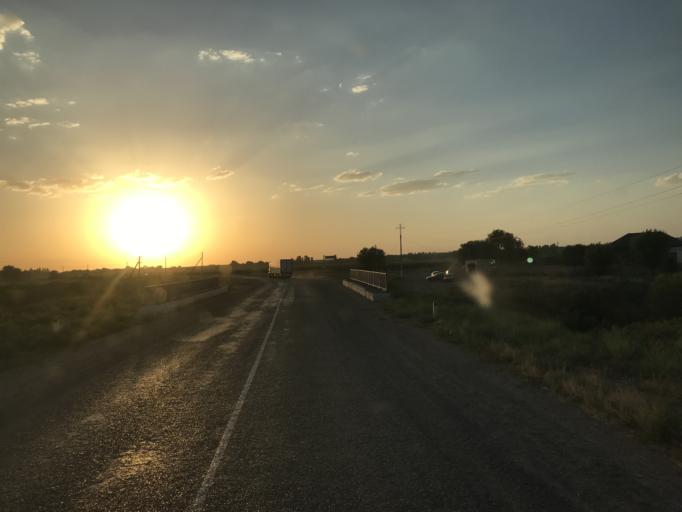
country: UZ
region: Toshkent
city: Yangiyul
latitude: 41.3744
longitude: 68.8263
